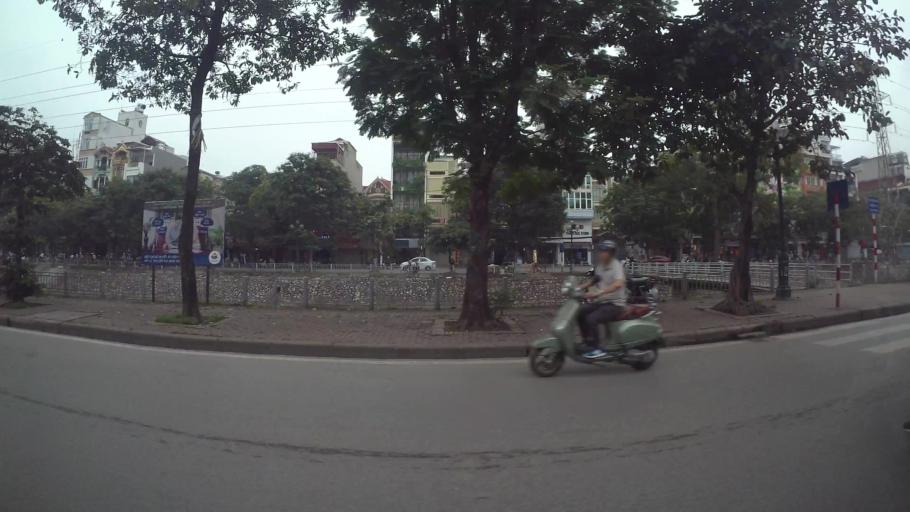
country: VN
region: Ha Noi
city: Hai BaTrung
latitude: 21.0005
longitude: 105.8615
